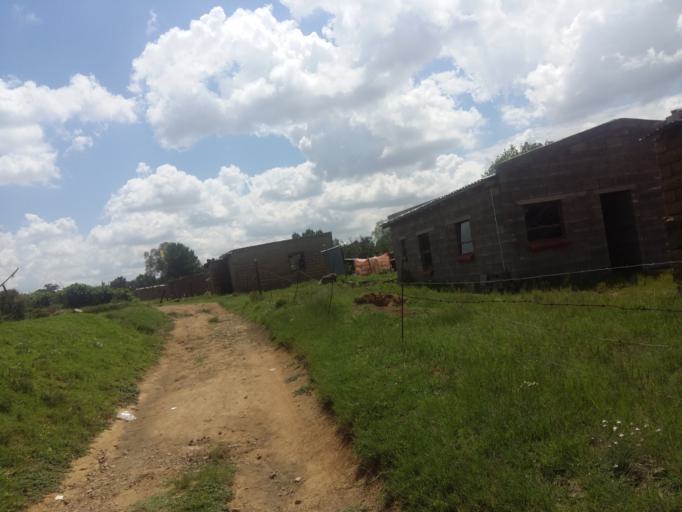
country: LS
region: Mafeteng
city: Mafeteng
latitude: -29.7594
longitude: 27.1119
